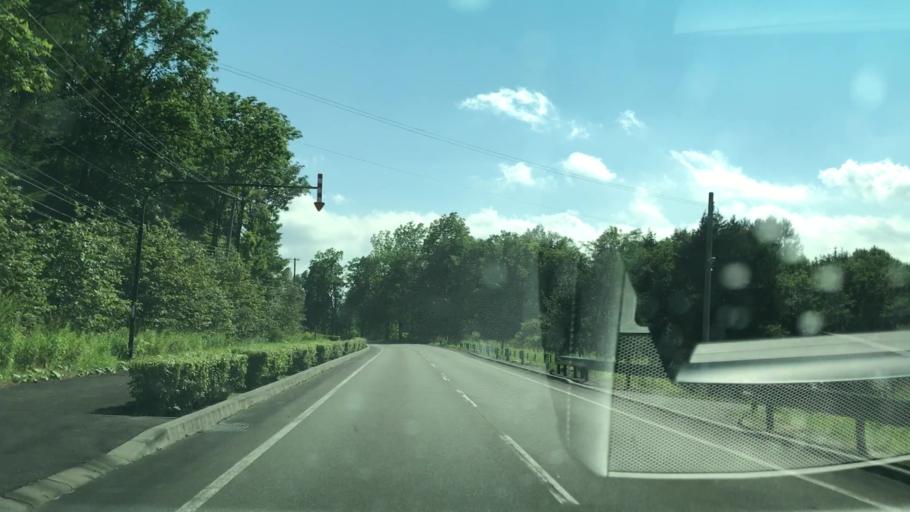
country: JP
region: Hokkaido
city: Shimo-furano
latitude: 42.8679
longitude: 142.4411
